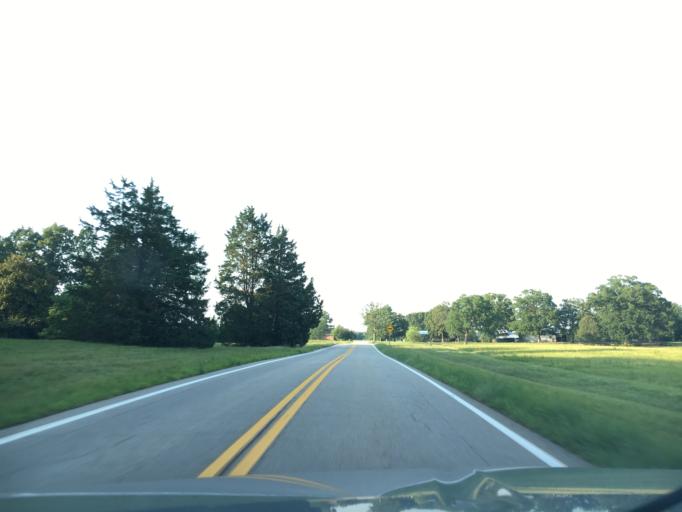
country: US
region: Virginia
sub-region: Pittsylvania County
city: Chatham
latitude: 36.8370
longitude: -79.2268
